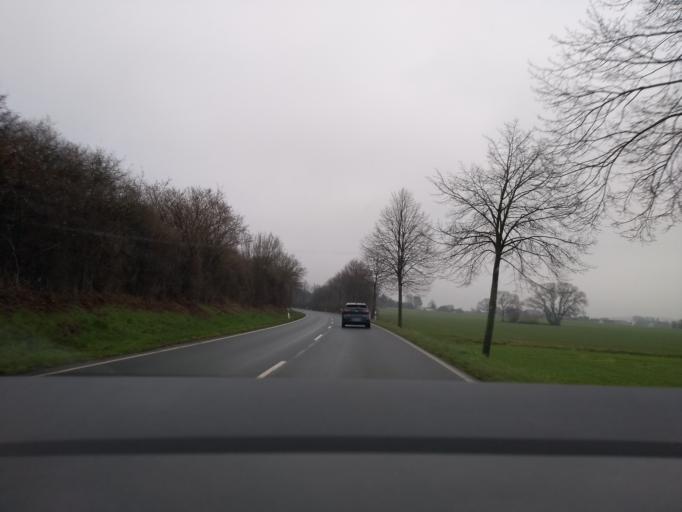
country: DE
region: North Rhine-Westphalia
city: Selm
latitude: 51.6603
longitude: 7.4745
